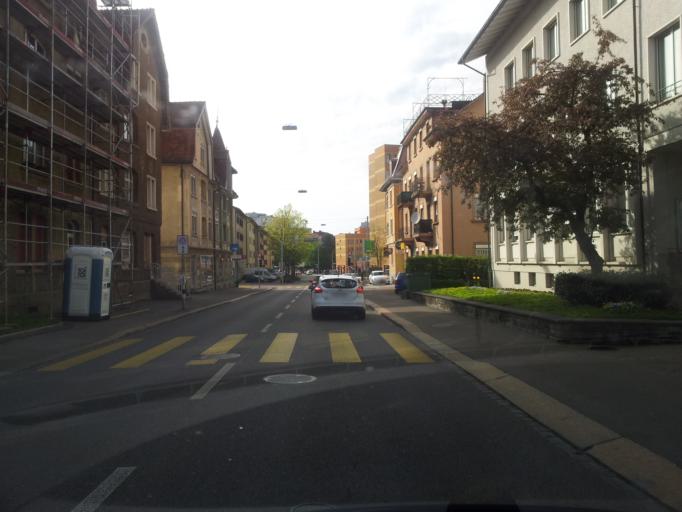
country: CH
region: Zurich
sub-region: Bezirk Zuerich
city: Zuerich (Kreis 11) / Oerlikon
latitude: 47.4066
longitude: 8.5516
